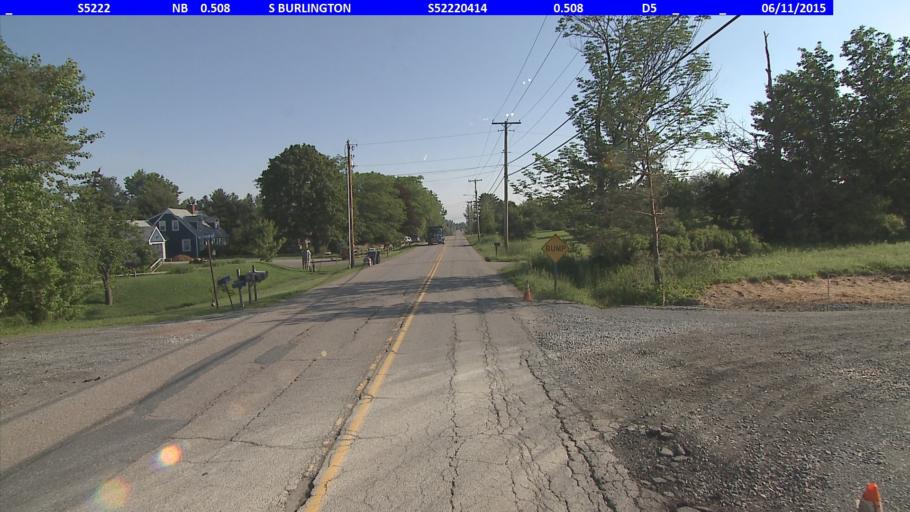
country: US
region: Vermont
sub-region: Chittenden County
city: South Burlington
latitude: 44.4241
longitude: -73.1952
